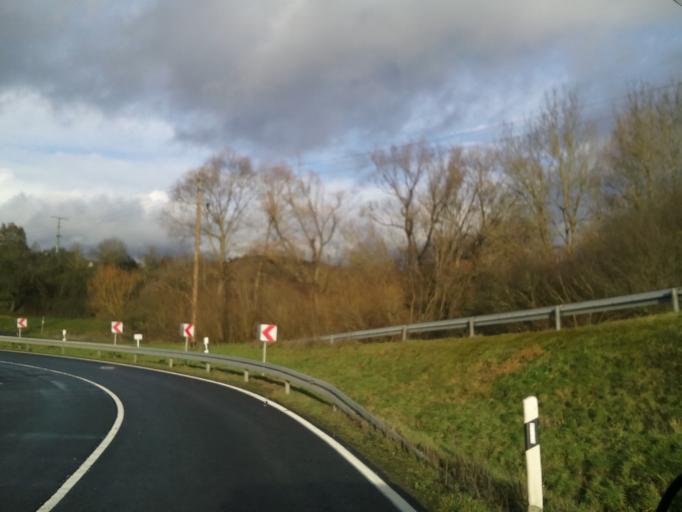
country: DE
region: Bavaria
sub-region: Regierungsbezirk Unterfranken
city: Gossenheim
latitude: 50.0123
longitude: 9.7891
